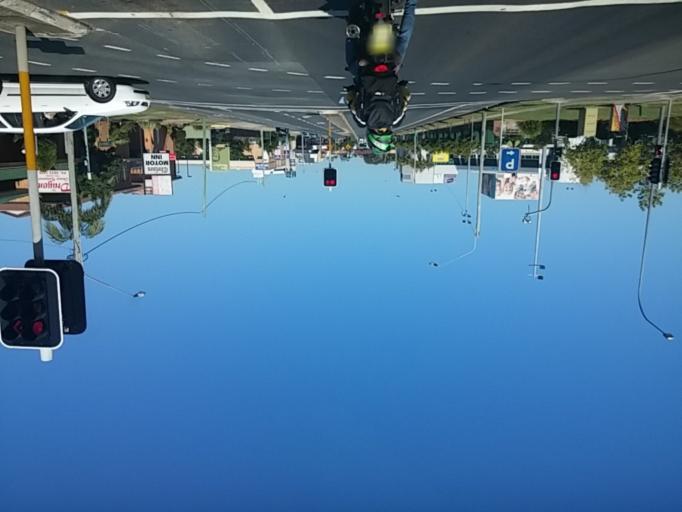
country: AU
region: New South Wales
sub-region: Coffs Harbour
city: Coffs Harbour
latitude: -30.2940
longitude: 153.1161
